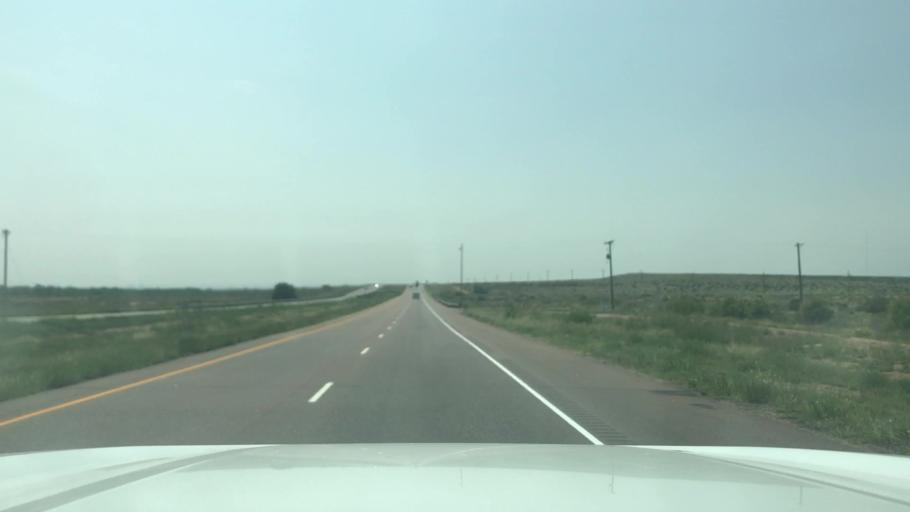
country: US
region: Colorado
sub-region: Pueblo County
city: Pueblo West
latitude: 38.3783
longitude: -104.6195
